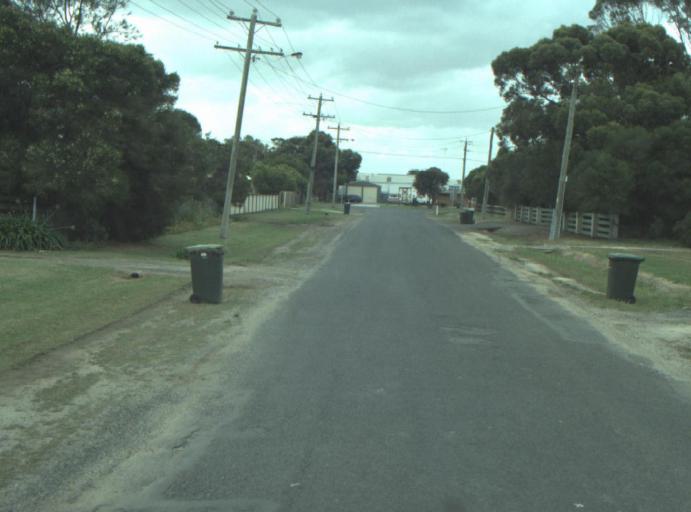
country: AU
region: Victoria
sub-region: Greater Geelong
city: East Geelong
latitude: -38.1700
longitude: 144.4078
